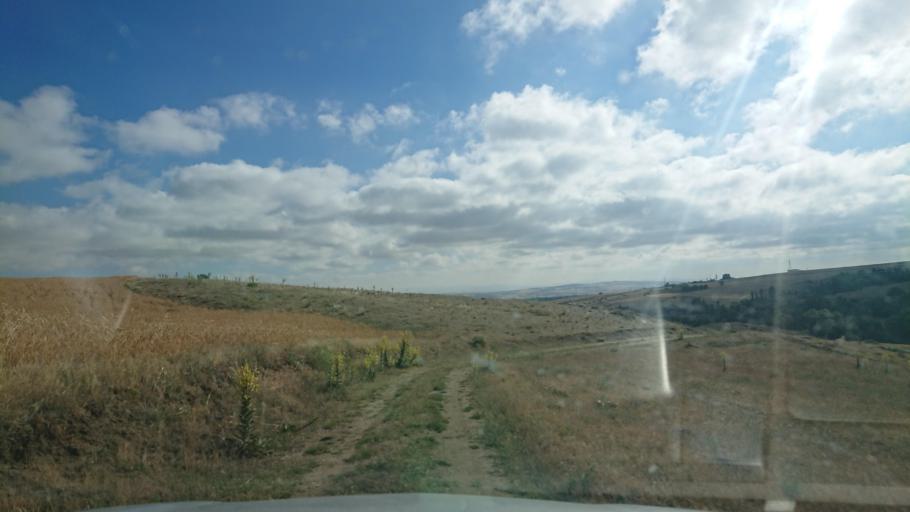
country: TR
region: Aksaray
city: Agacoren
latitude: 38.8502
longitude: 33.9287
